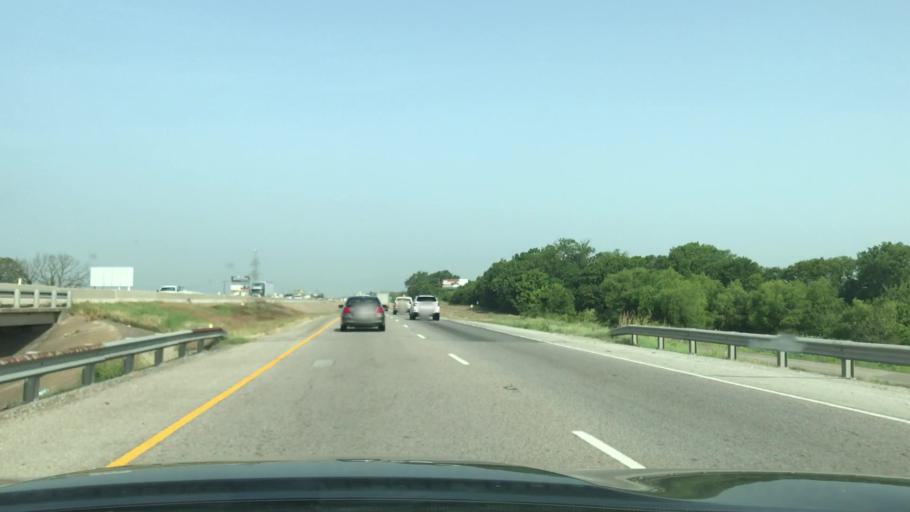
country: US
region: Texas
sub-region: Kaufman County
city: Forney
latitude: 32.7756
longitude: -96.5081
